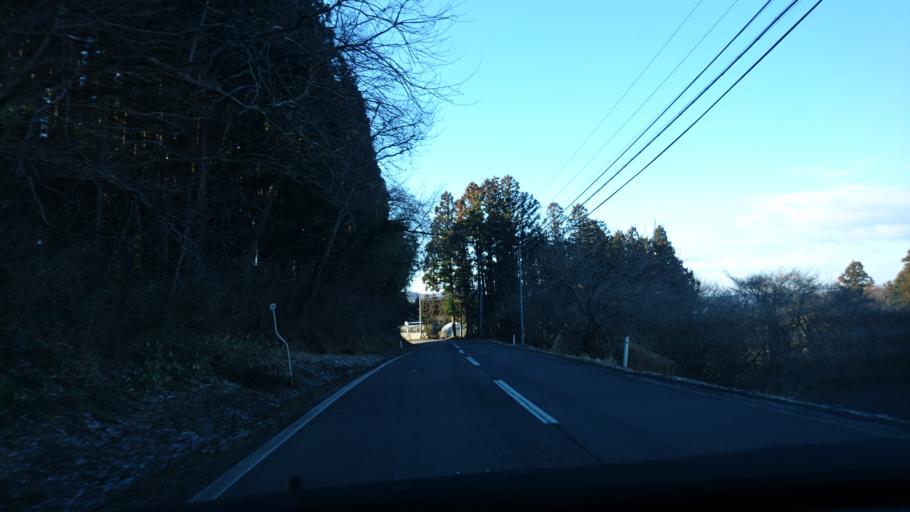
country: JP
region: Iwate
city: Ichinoseki
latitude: 38.8633
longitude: 141.2983
